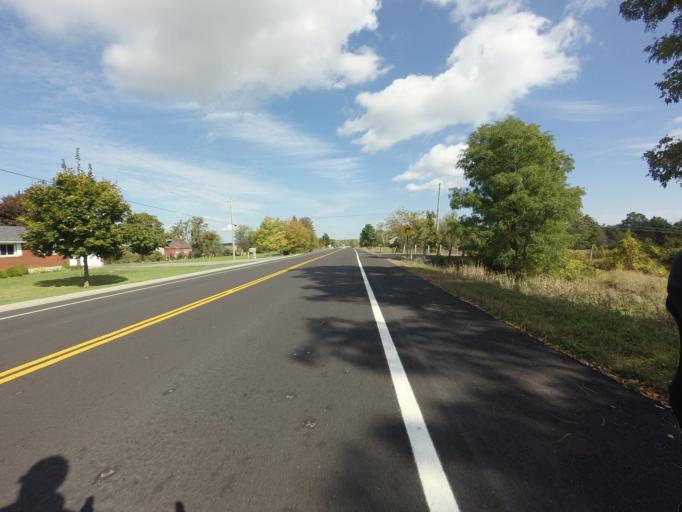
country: CA
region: Ontario
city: Napanee Downtown
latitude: 44.1242
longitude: -76.8942
